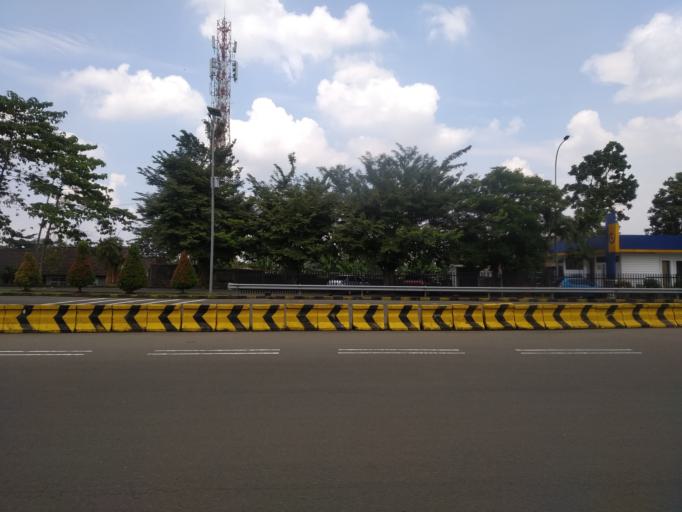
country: ID
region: West Java
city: Bogor
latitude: -6.5978
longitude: 106.8170
